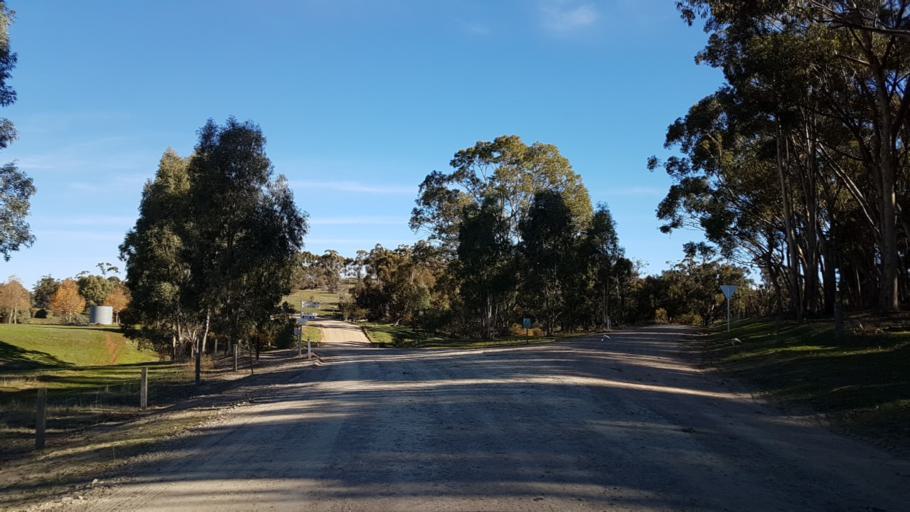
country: AU
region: South Australia
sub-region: Northern Areas
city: Jamestown
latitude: -33.2851
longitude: 138.5659
